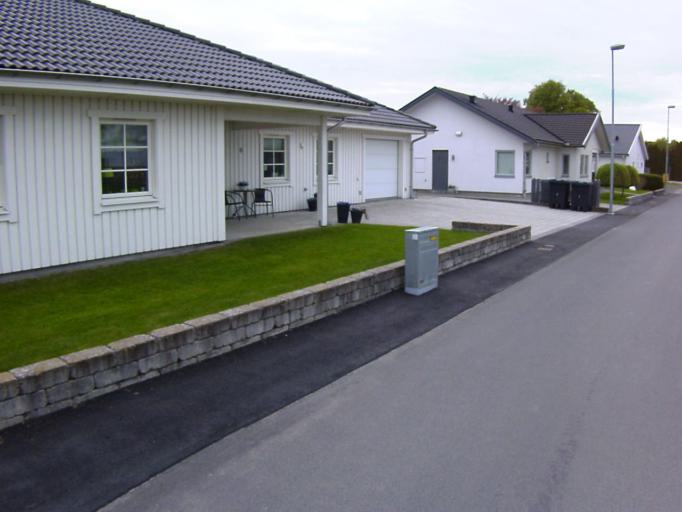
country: SE
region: Skane
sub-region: Kristianstads Kommun
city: Kristianstad
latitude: 56.0176
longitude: 14.1961
